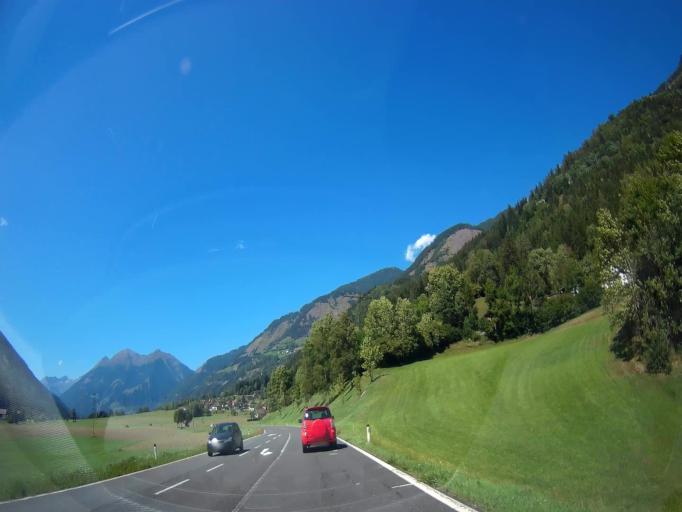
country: AT
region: Carinthia
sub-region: Politischer Bezirk Spittal an der Drau
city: Obervellach
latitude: 46.9044
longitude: 13.2577
